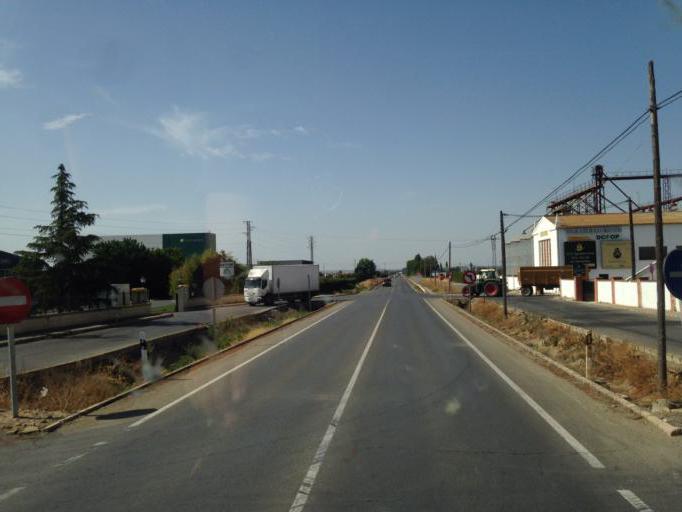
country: ES
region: Andalusia
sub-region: Provincia de Malaga
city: Antequera
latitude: 37.0342
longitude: -4.5611
